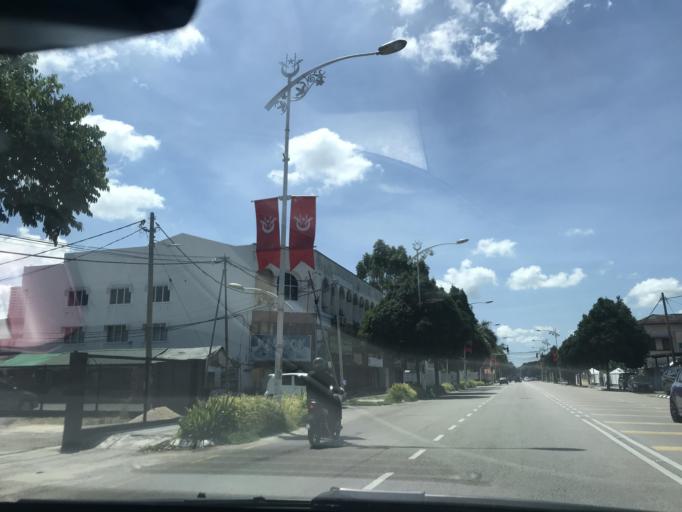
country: MY
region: Kelantan
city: Kota Bharu
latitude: 6.1089
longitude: 102.2448
